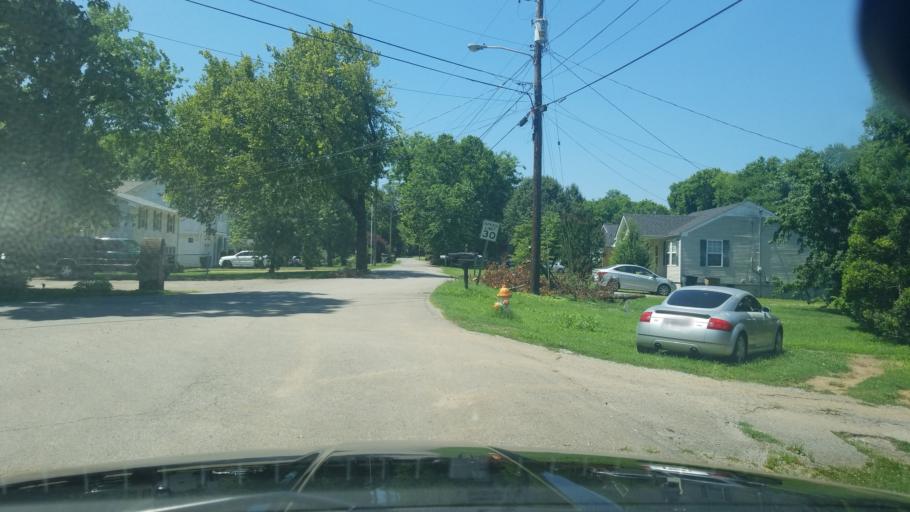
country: US
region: Tennessee
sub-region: Davidson County
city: Belle Meade
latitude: 36.1644
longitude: -86.8713
